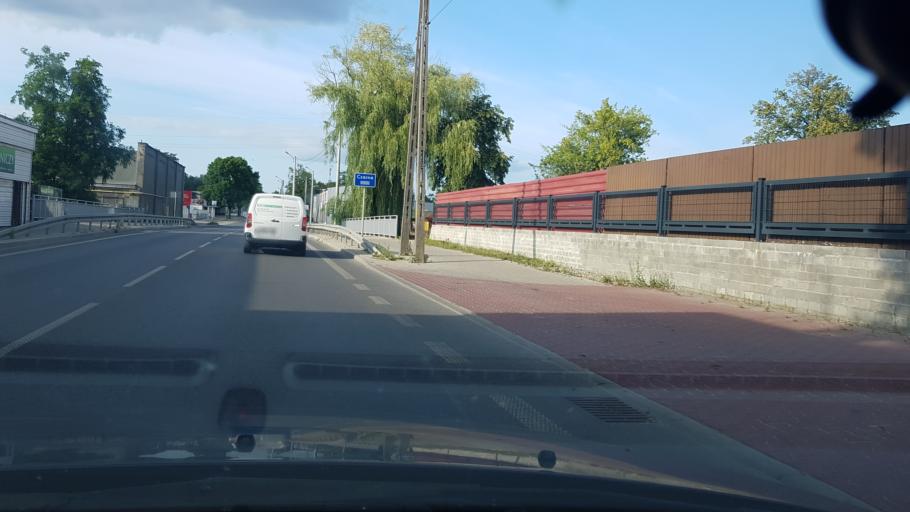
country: PL
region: Lodz Voivodeship
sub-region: Powiat tomaszowski
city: Tomaszow Mazowiecki
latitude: 51.5491
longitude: 20.0157
